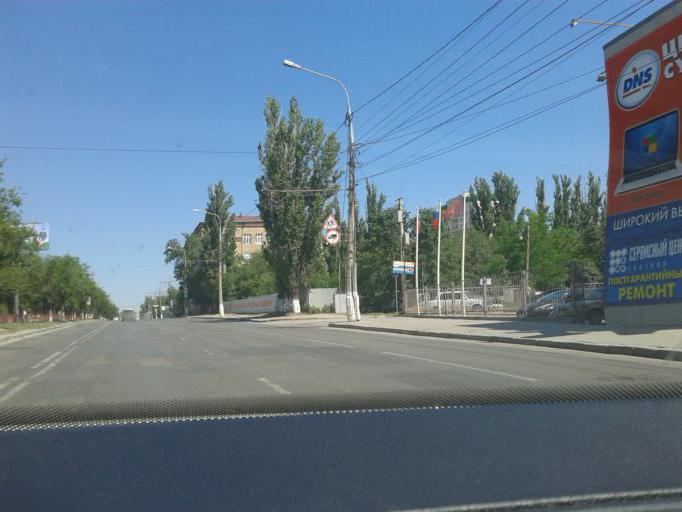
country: RU
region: Volgograd
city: Volgograd
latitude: 48.7316
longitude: 44.4970
